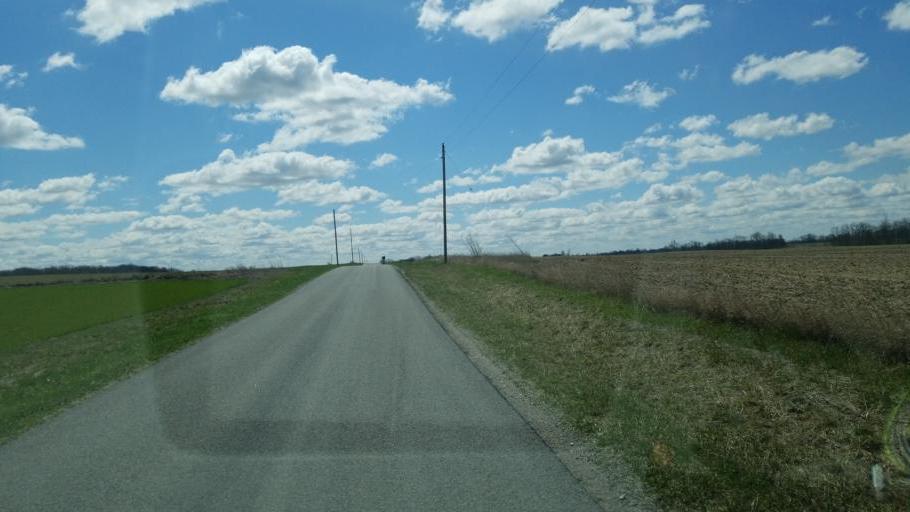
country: US
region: Ohio
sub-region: Hancock County
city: Findlay
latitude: 41.0581
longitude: -83.5149
